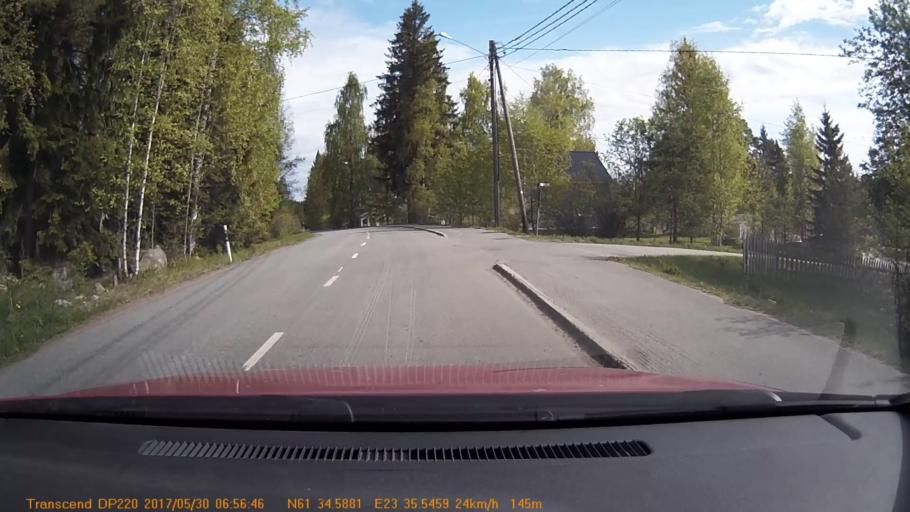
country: FI
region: Pirkanmaa
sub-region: Tampere
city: Yloejaervi
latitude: 61.5763
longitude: 23.5924
